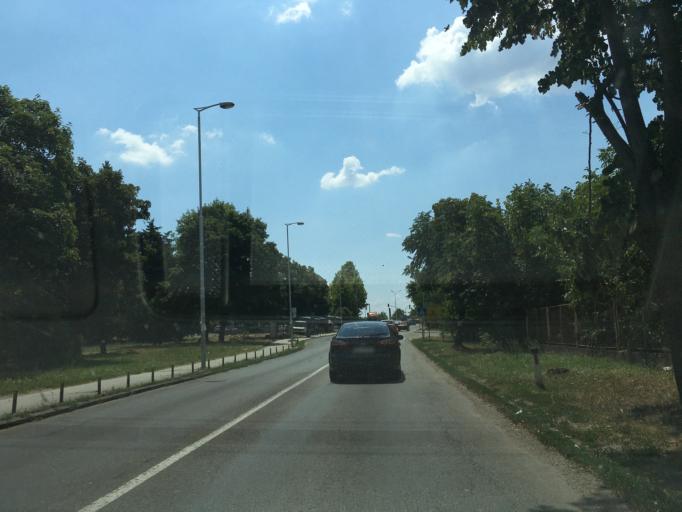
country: RS
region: Central Serbia
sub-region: Belgrade
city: Mladenovac
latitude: 44.4490
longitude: 20.6862
